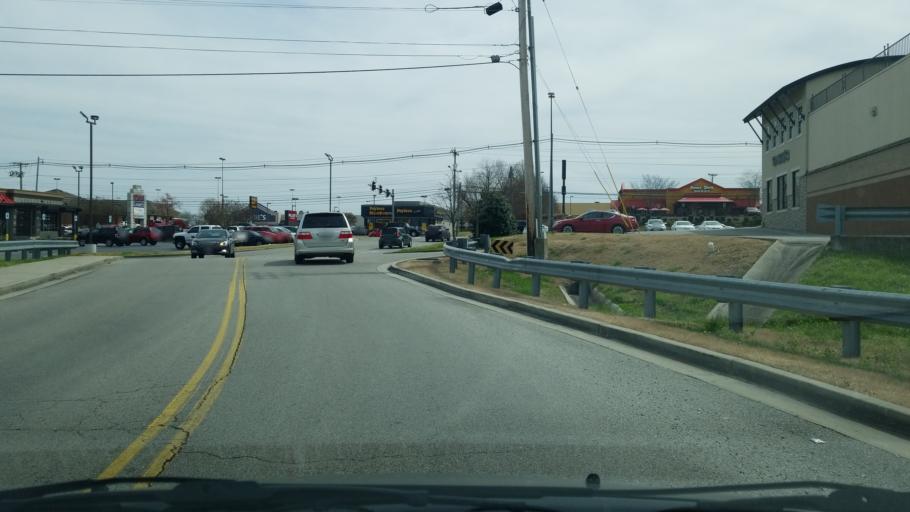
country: US
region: Tennessee
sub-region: Hamilton County
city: East Brainerd
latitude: 35.0352
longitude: -85.1539
